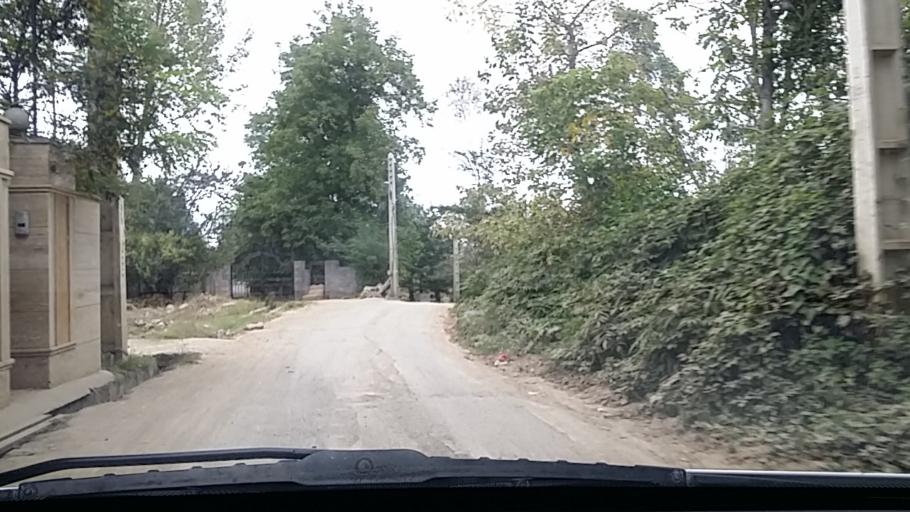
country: IR
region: Mazandaran
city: `Abbasabad
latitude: 36.5136
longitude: 51.1632
